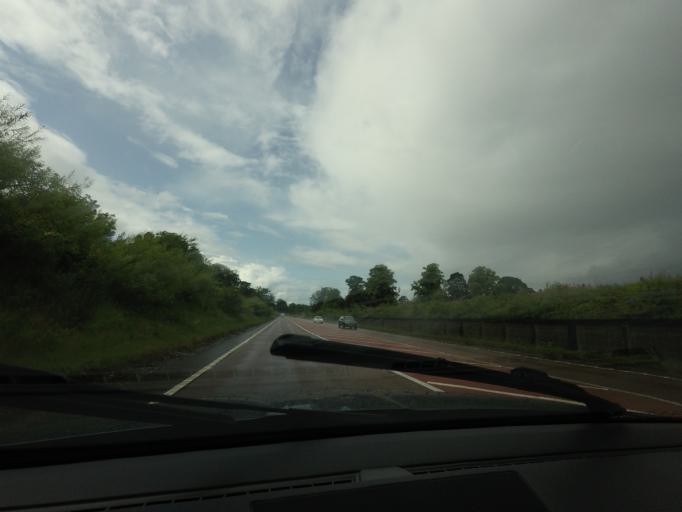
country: GB
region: Scotland
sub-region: Moray
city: Fochabers
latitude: 57.6149
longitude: -3.0938
